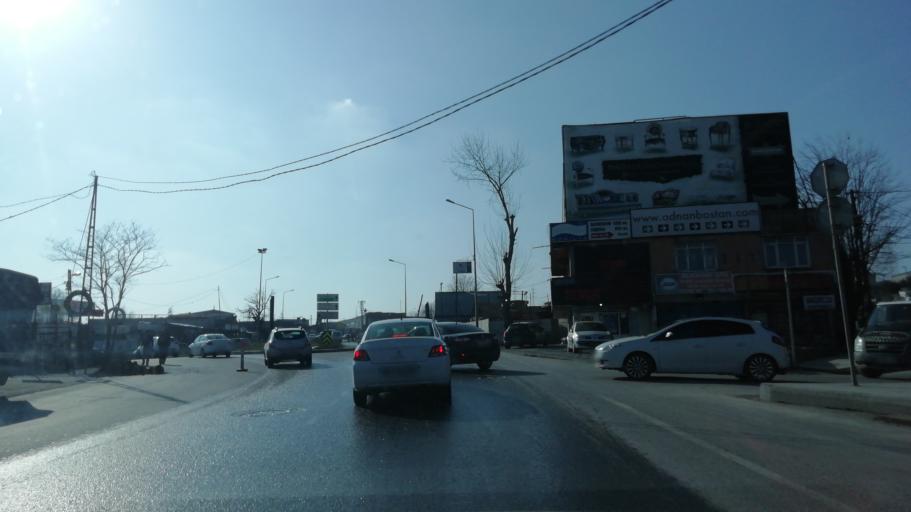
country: TR
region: Istanbul
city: Basaksehir
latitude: 41.0635
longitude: 28.7415
